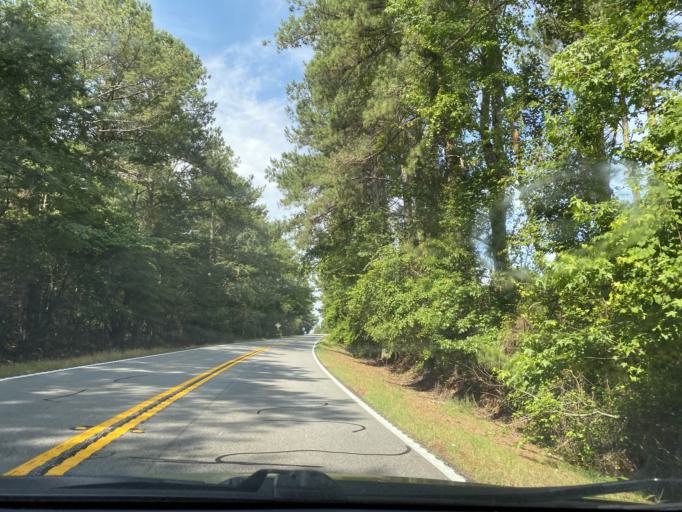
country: US
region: Georgia
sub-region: Coweta County
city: Grantville
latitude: 33.2460
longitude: -84.7297
